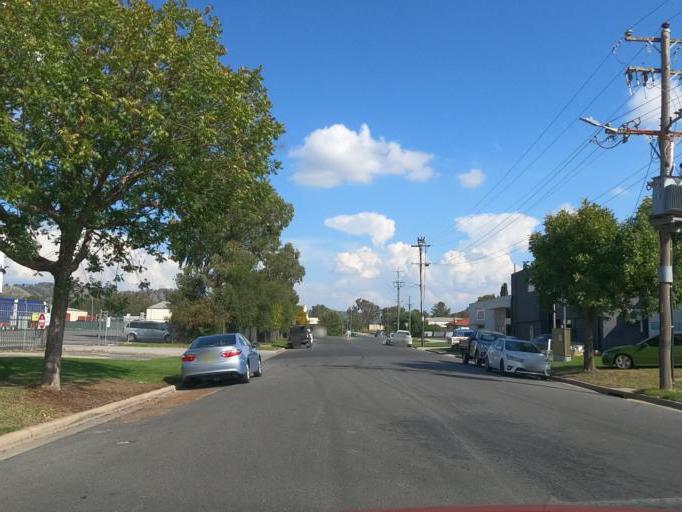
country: AU
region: New South Wales
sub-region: Albury Municipality
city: South Albury
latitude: -36.0925
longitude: 146.9201
